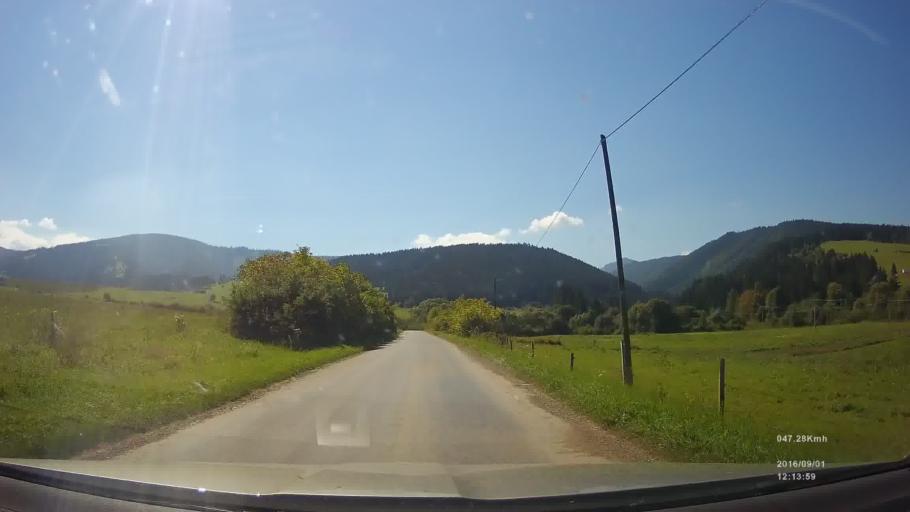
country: SK
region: Zilinsky
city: Ruzomberok
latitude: 49.0500
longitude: 19.4303
